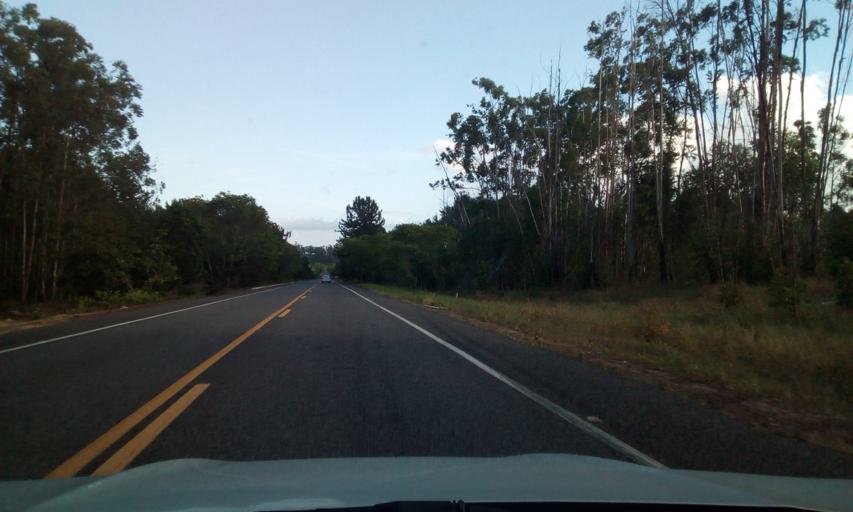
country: BR
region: Bahia
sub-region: Entre Rios
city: Entre Rios
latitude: -12.3174
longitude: -37.9044
